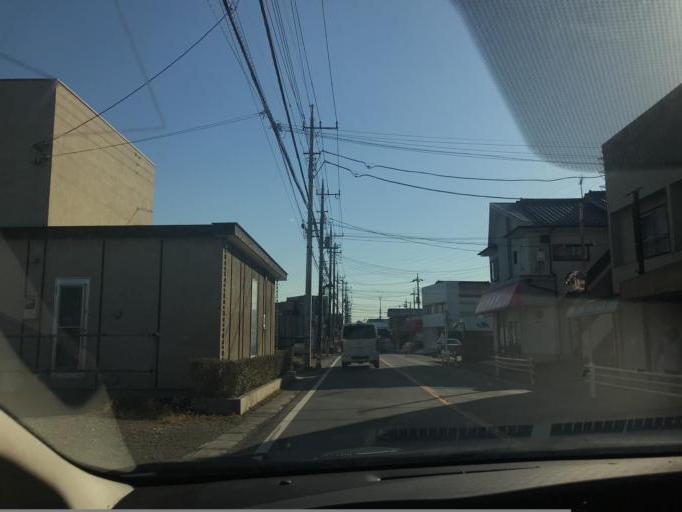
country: JP
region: Saitama
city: Yashio-shi
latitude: 35.8374
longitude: 139.8362
